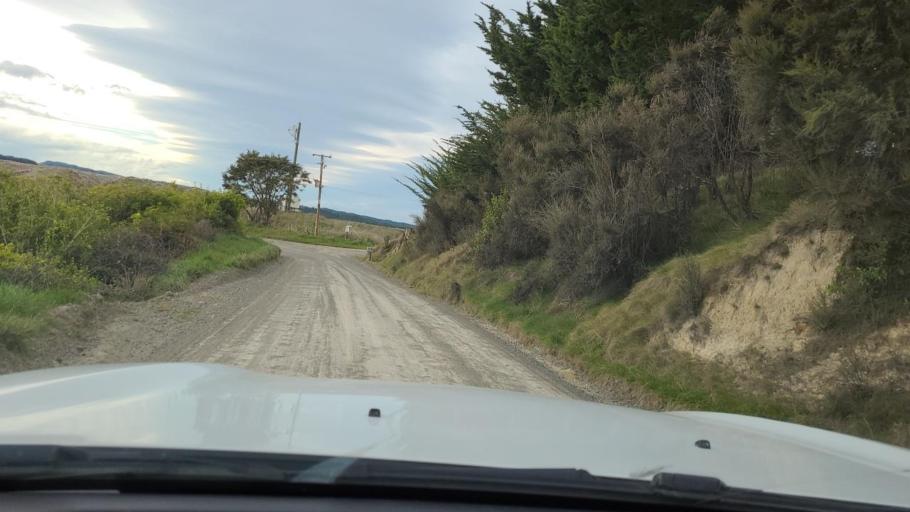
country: NZ
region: Hawke's Bay
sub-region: Napier City
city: Napier
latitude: -39.3202
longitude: 176.8403
